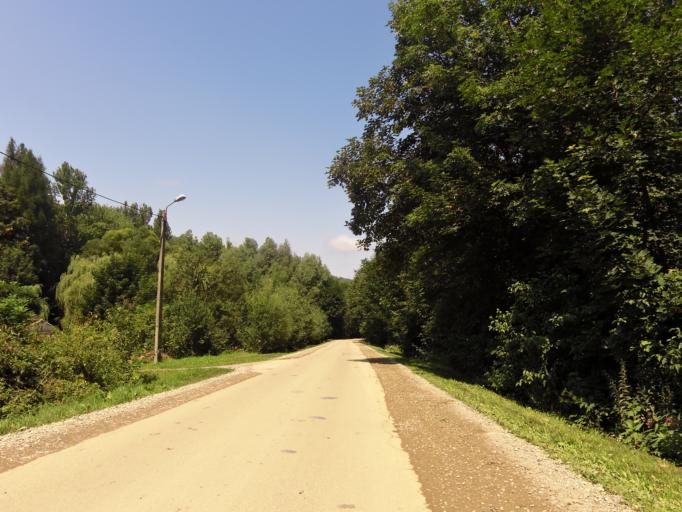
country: PL
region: Silesian Voivodeship
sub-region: Powiat zywiecki
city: Cisiec
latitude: 49.5929
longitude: 19.0982
